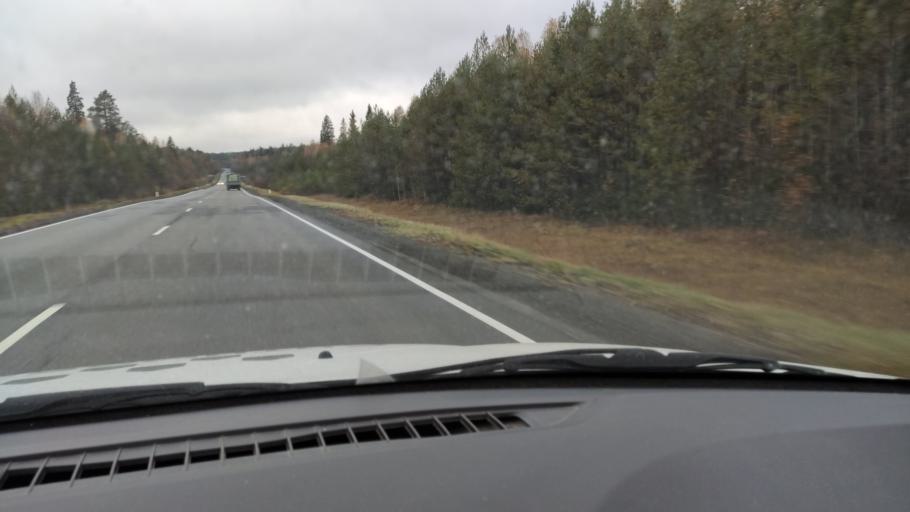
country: RU
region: Kirov
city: Dubrovka
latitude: 58.9048
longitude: 51.2710
